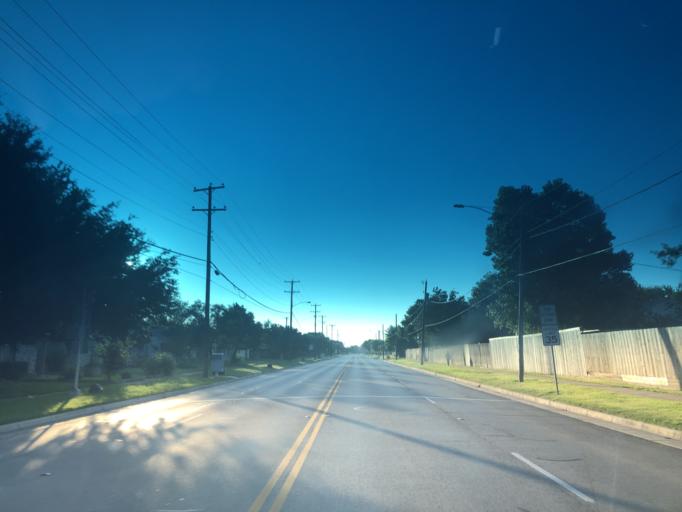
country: US
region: Texas
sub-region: Dallas County
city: Grand Prairie
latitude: 32.6981
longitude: -97.0112
